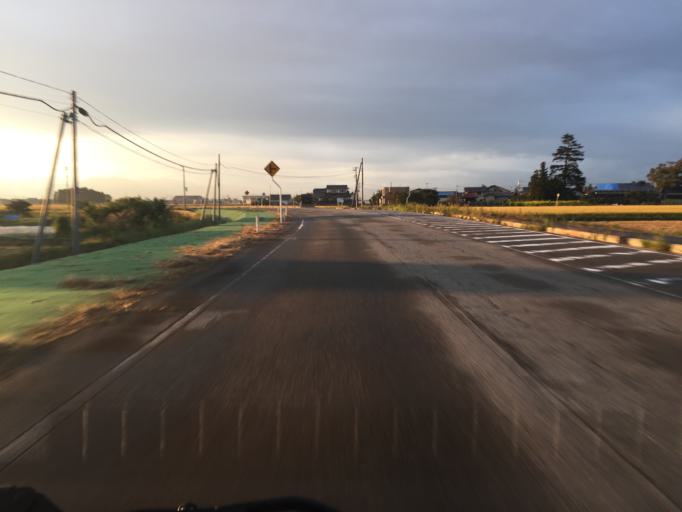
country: JP
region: Fukushima
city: Kitakata
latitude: 37.5623
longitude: 139.8891
